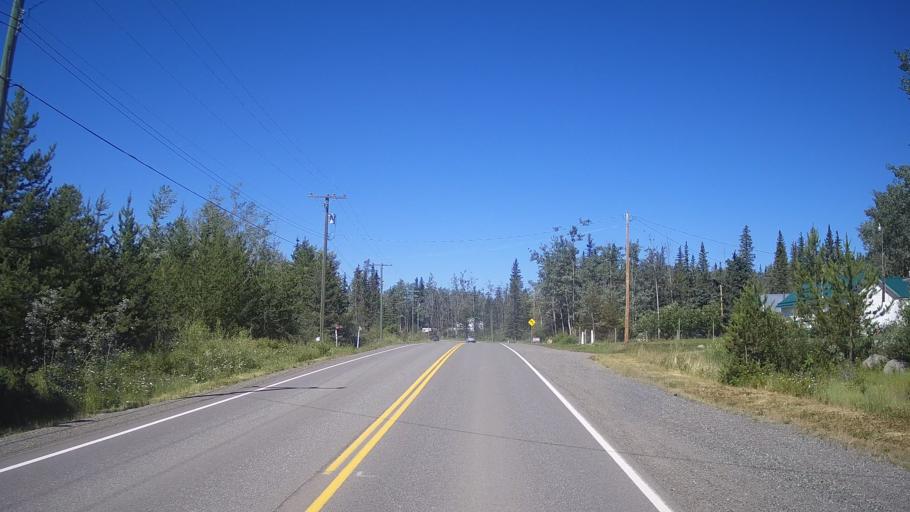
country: CA
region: British Columbia
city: Cache Creek
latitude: 51.5547
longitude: -121.2164
